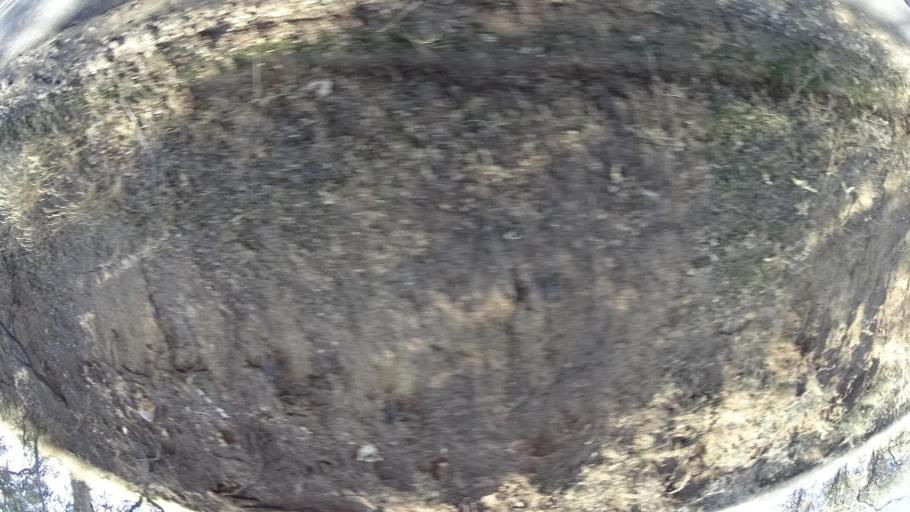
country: US
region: California
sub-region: Kern County
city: Bear Valley Springs
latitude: 35.3365
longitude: -118.5760
